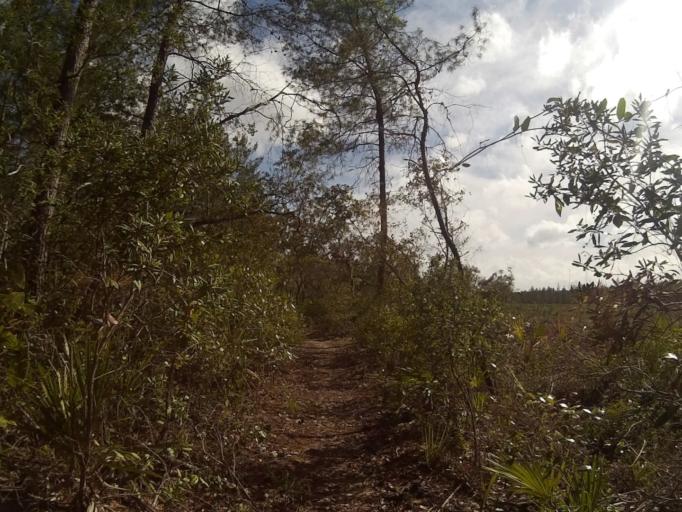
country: US
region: Florida
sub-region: Lake County
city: Astor
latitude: 29.0664
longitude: -81.6077
